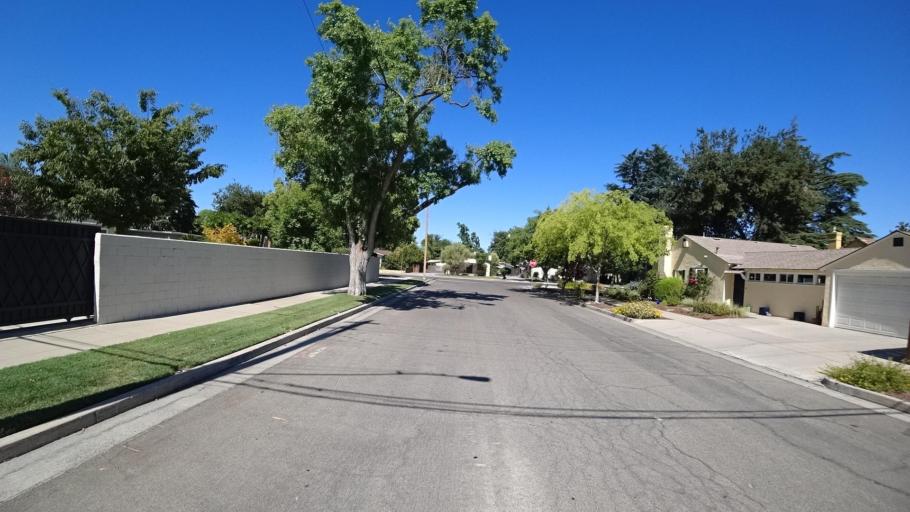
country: US
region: California
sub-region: Fresno County
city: Fresno
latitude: 36.7730
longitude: -119.8115
